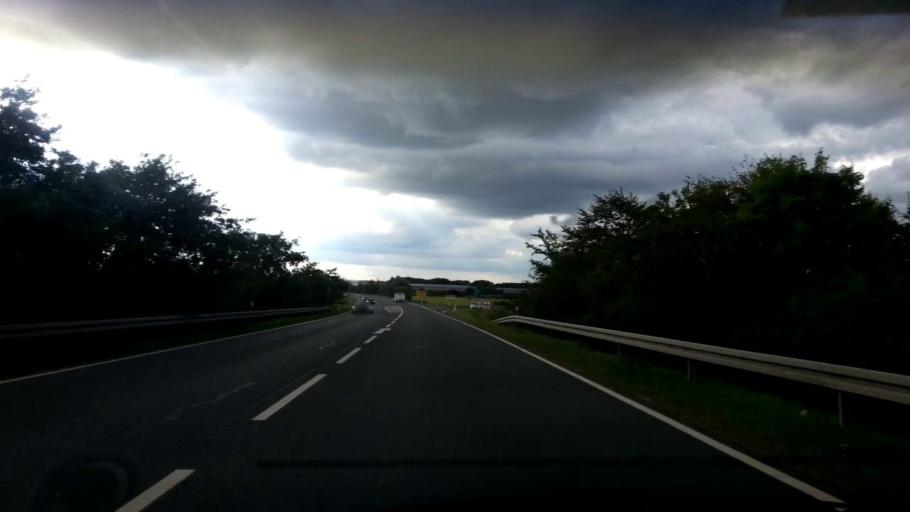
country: DE
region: Bavaria
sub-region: Regierungsbezirk Mittelfranken
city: Adelsdorf
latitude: 49.7017
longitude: 10.8817
